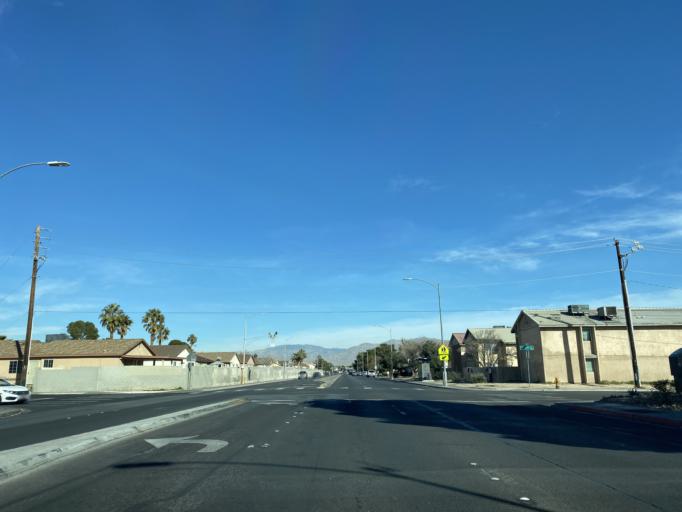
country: US
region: Nevada
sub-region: Clark County
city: Las Vegas
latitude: 36.1984
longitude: -115.2238
